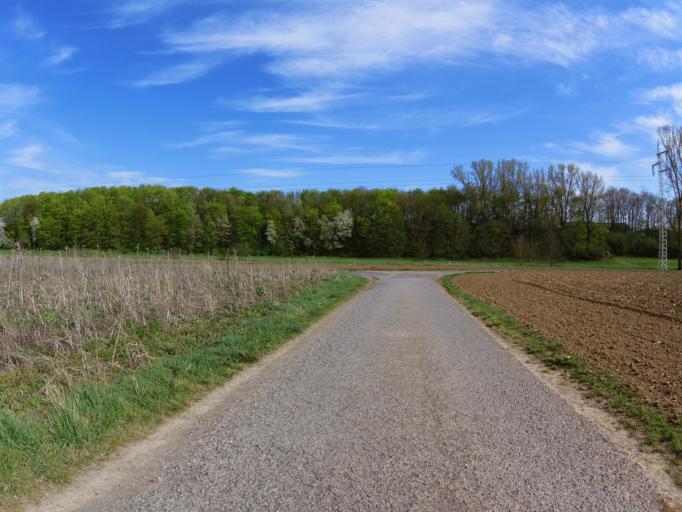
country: DE
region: Bavaria
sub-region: Regierungsbezirk Unterfranken
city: Unterpleichfeld
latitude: 49.8653
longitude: 10.0312
